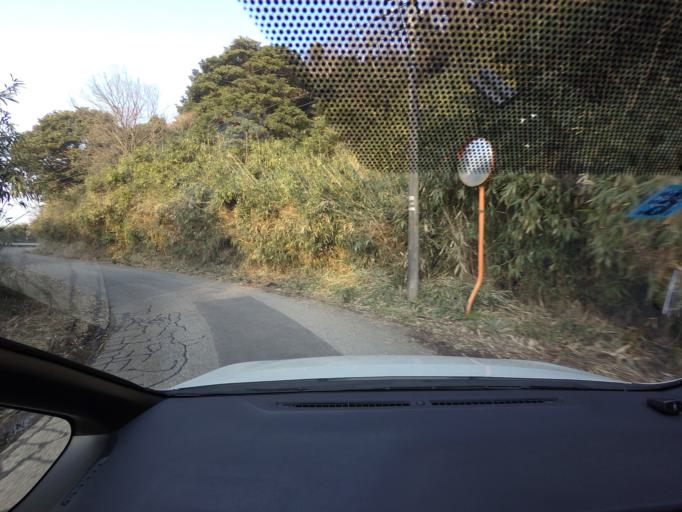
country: JP
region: Ishikawa
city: Nanao
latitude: 37.1437
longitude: 137.0161
